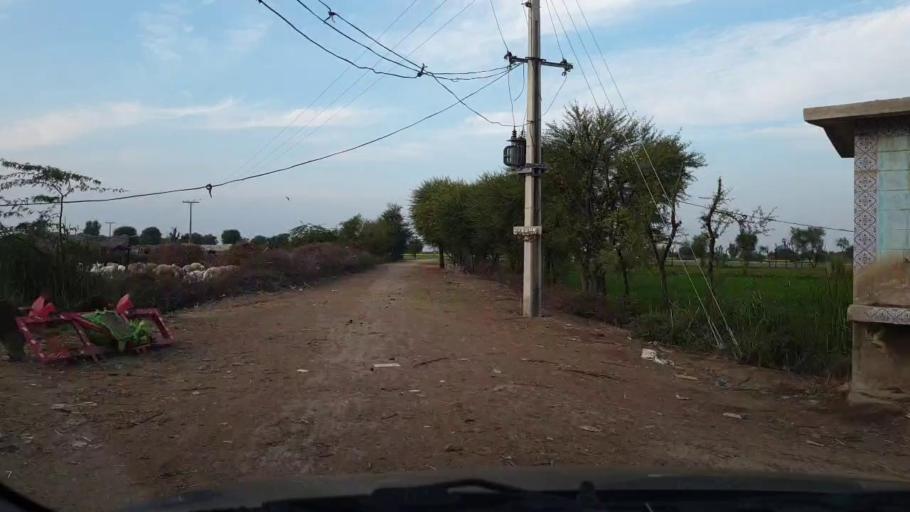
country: PK
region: Sindh
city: Jhol
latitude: 25.9805
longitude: 68.8633
